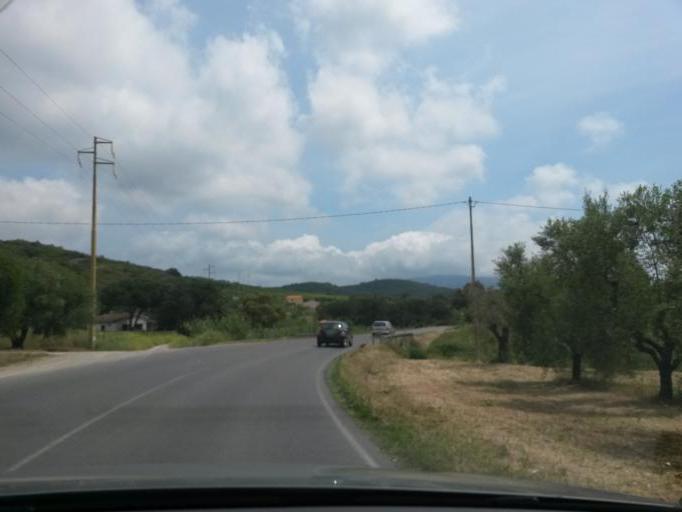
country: IT
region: Tuscany
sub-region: Provincia di Livorno
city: Capoliveri
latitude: 42.7788
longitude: 10.3480
